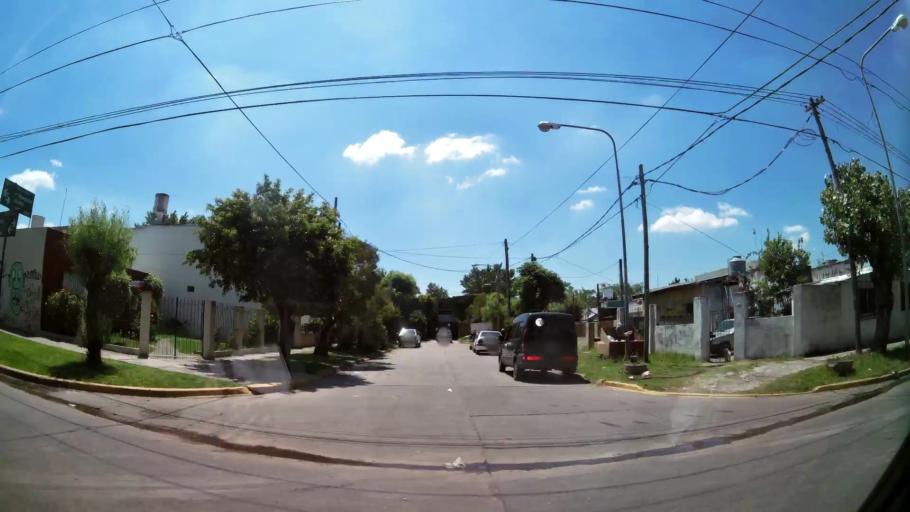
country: AR
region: Buenos Aires
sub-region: Partido de Tigre
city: Tigre
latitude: -34.4393
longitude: -58.5809
